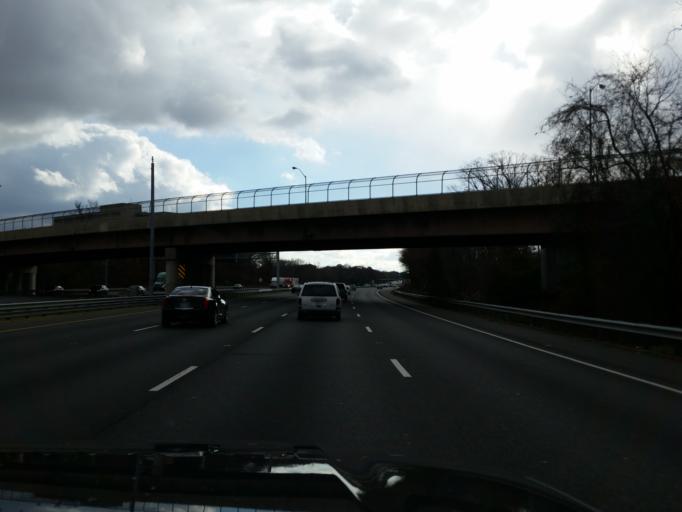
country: US
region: Maryland
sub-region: Prince George's County
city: Berwyn Heights
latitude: 39.0104
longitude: -76.9023
